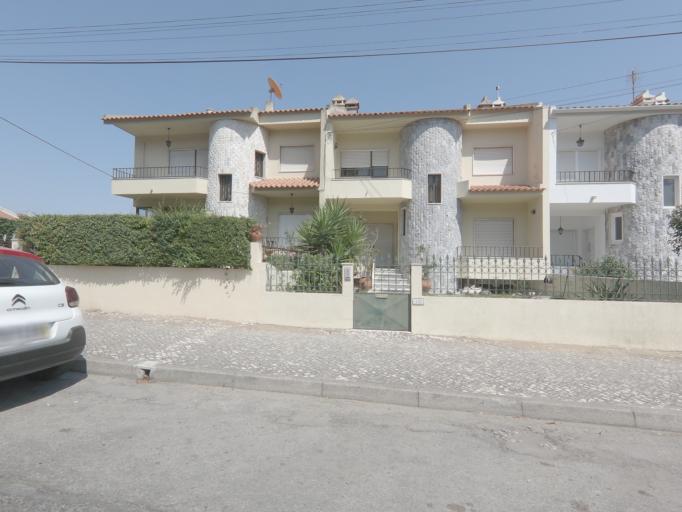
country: PT
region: Setubal
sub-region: Palmela
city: Palmela
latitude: 38.5722
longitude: -8.8886
